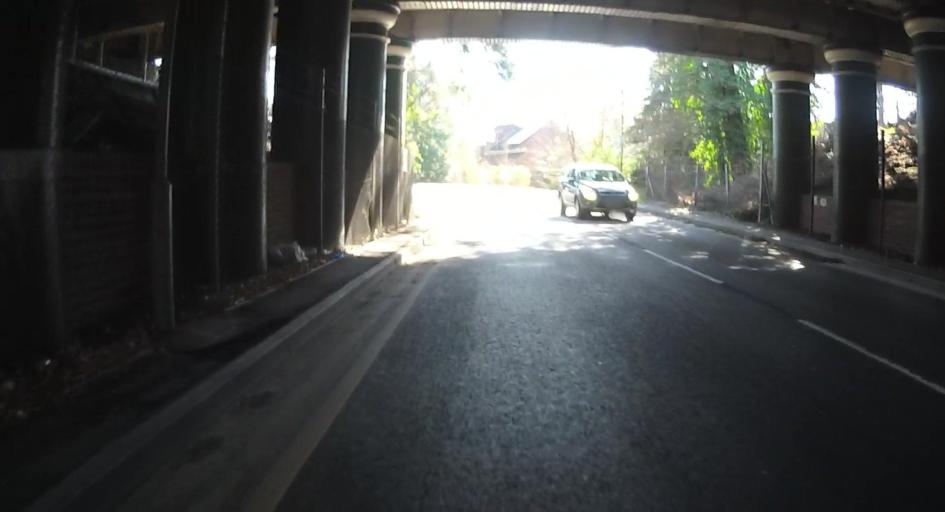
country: GB
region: England
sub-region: Royal Borough of Windsor and Maidenhead
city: Ascot
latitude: 51.4053
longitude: -0.6721
